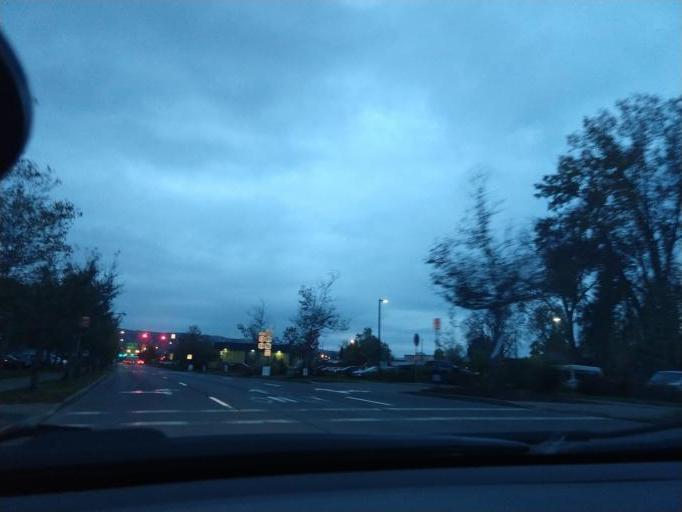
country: US
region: New York
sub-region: Tompkins County
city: Ithaca
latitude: 42.4432
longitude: -76.5107
